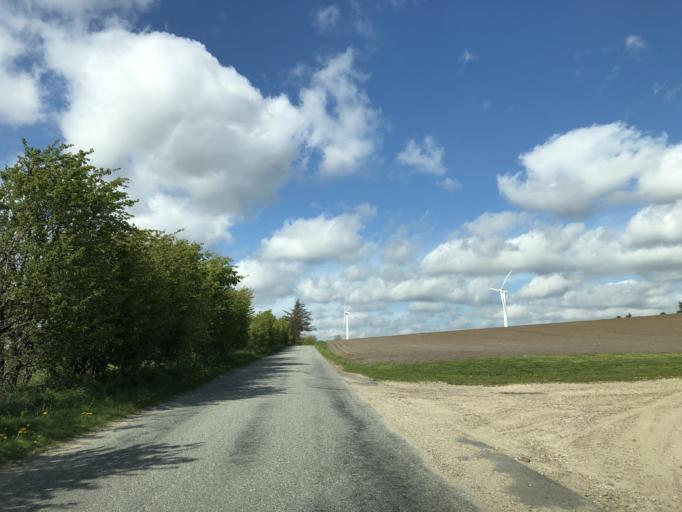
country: DK
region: Central Jutland
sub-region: Herning Kommune
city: Avlum
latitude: 56.2786
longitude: 8.6960
